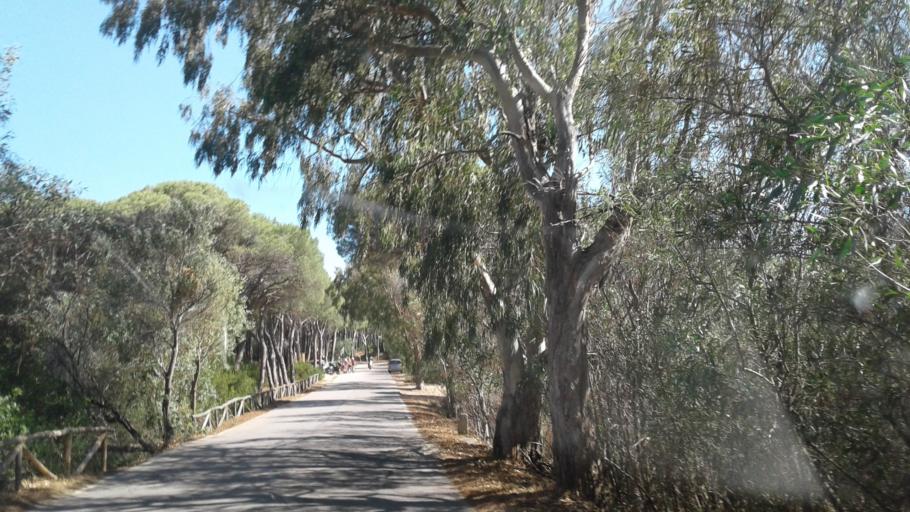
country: IT
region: Sardinia
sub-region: Provincia di Olbia-Tempio
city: La Maddalena
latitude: 41.2123
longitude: 9.4551
